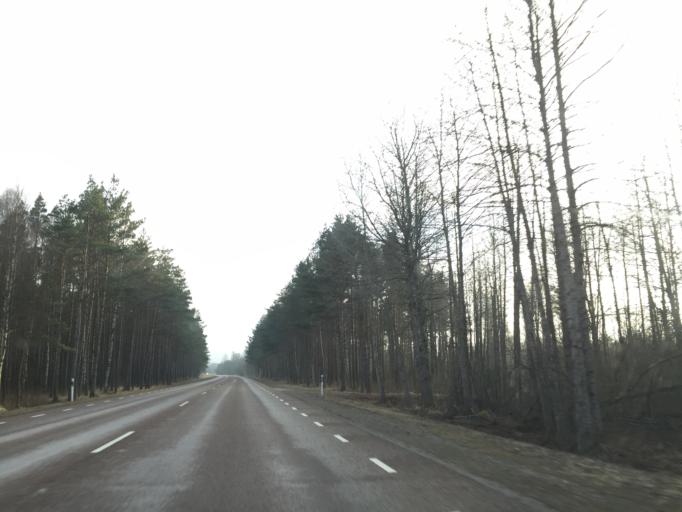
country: EE
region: Saare
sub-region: Kuressaare linn
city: Kuressaare
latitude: 58.3676
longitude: 22.7235
